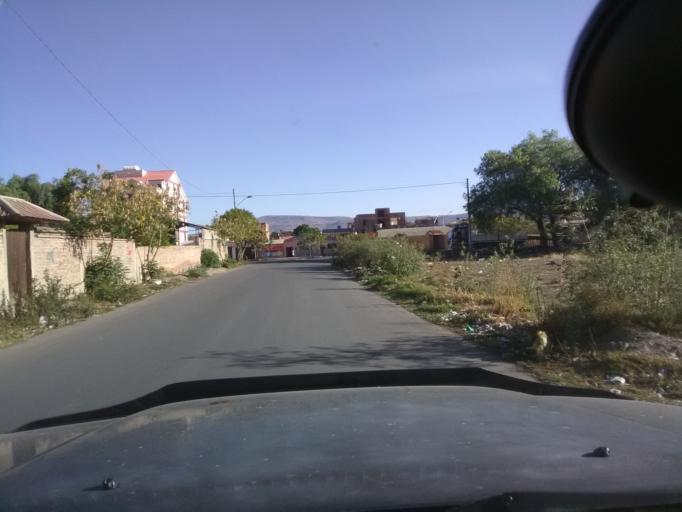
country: BO
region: Cochabamba
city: Cochabamba
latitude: -17.3805
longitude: -66.2008
